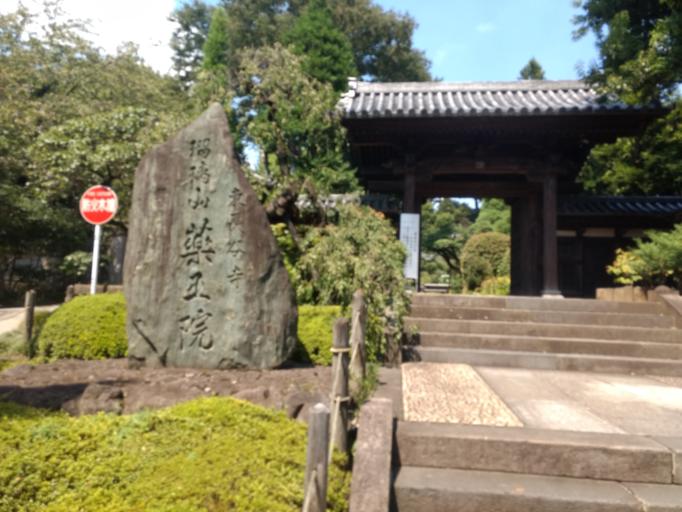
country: JP
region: Tokyo
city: Tokyo
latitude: 35.7170
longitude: 139.6975
